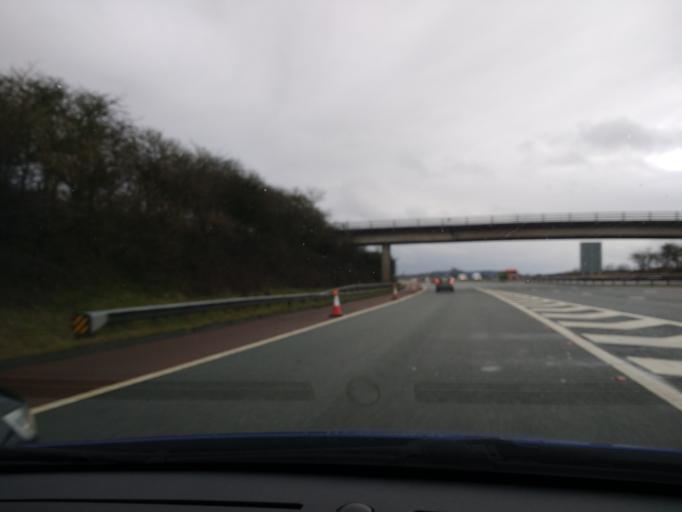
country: GB
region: England
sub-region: Cumbria
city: Milnthorpe
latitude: 54.2332
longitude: -2.7194
